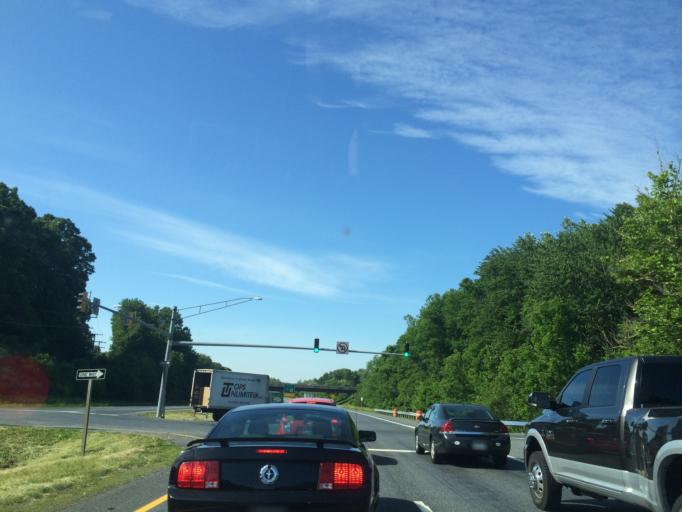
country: US
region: Maryland
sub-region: Carroll County
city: Sykesville
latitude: 39.3112
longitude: -76.9521
